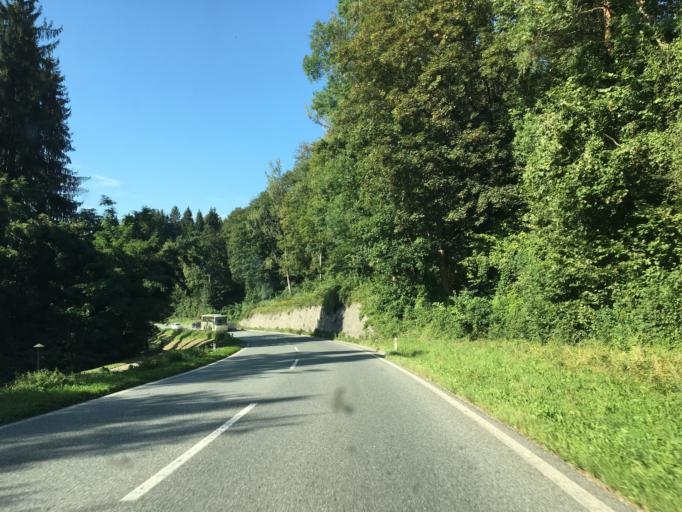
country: AT
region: Carinthia
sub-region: Politischer Bezirk Volkermarkt
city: Voelkermarkt
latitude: 46.6422
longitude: 14.6313
